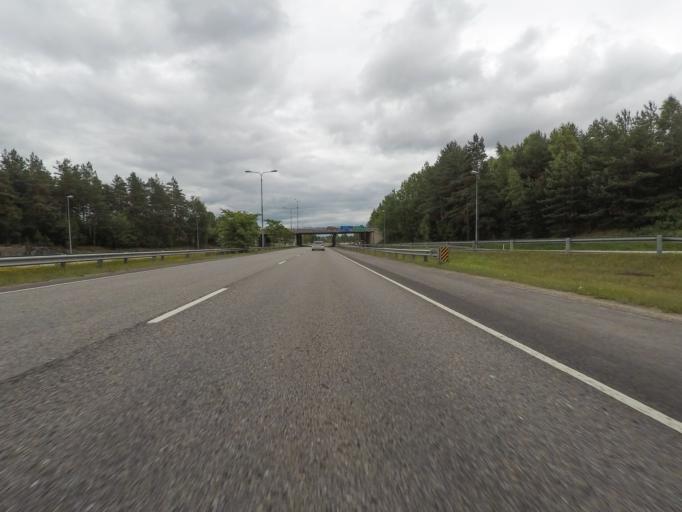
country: FI
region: Varsinais-Suomi
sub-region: Turku
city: Turku
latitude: 60.4975
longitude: 22.2788
